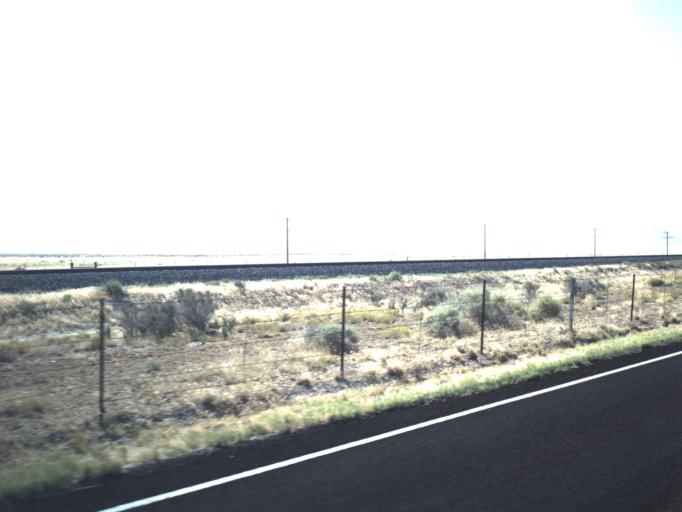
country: US
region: Utah
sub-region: Millard County
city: Delta
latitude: 38.9249
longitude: -112.8110
